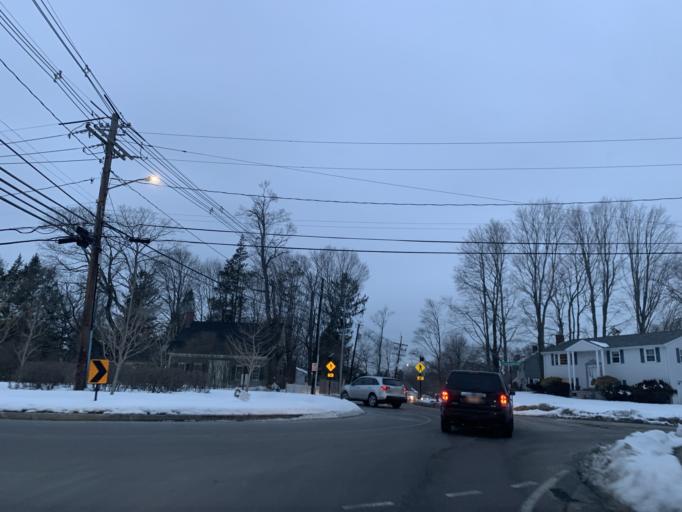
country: US
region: Massachusetts
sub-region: Norfolk County
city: Canton
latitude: 42.1507
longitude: -71.1278
